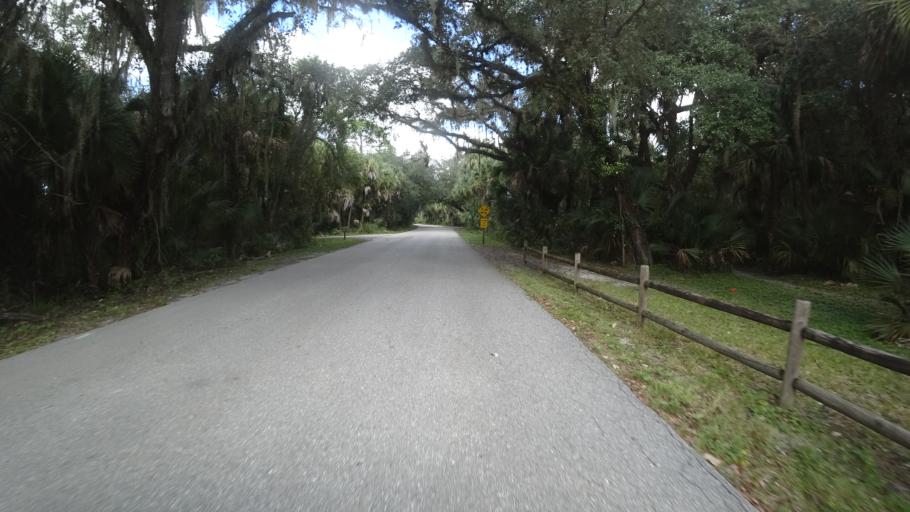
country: US
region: Florida
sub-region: Sarasota County
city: Lake Sarasota
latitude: 27.2420
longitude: -82.3142
